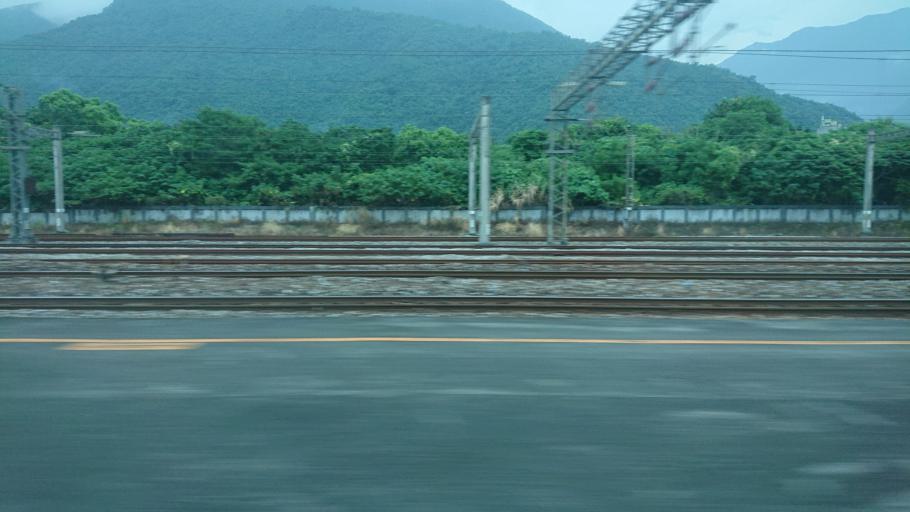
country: TW
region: Taiwan
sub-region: Hualien
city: Hualian
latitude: 24.1270
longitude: 121.6401
